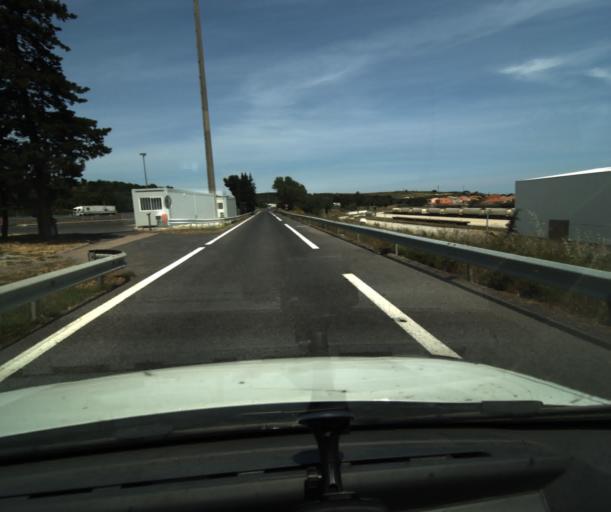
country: FR
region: Languedoc-Roussillon
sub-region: Departement des Pyrenees-Orientales
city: el Volo
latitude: 42.5276
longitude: 2.8232
